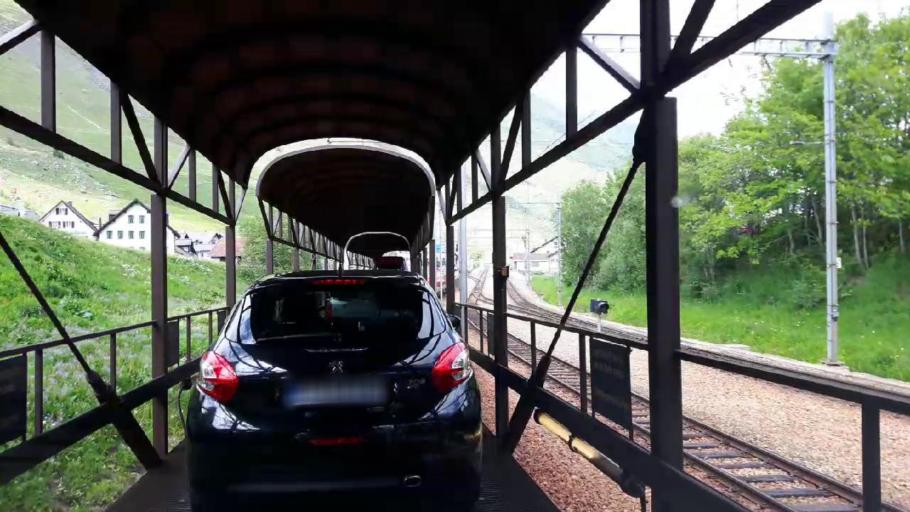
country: CH
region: Uri
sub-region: Uri
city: Andermatt
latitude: 46.5968
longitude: 8.5021
